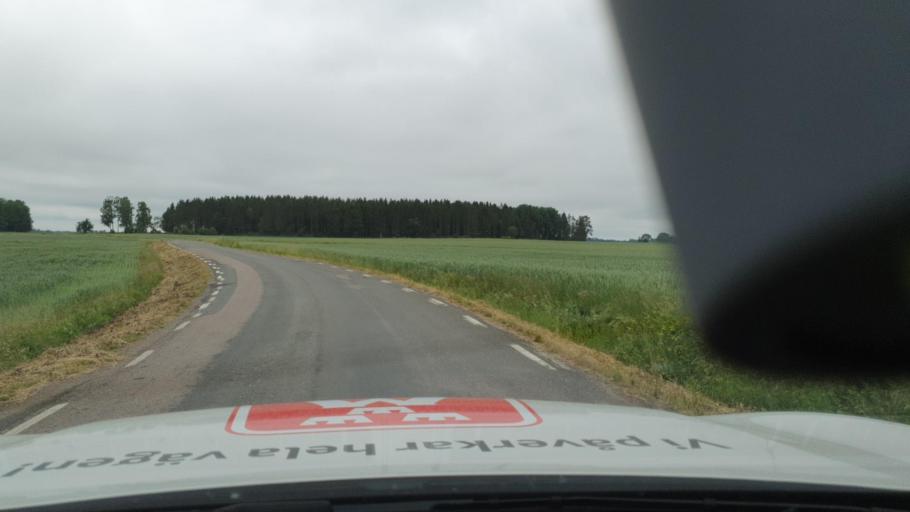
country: SE
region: Vaestra Goetaland
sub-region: Tibro Kommun
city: Tibro
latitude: 58.3655
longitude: 14.0836
